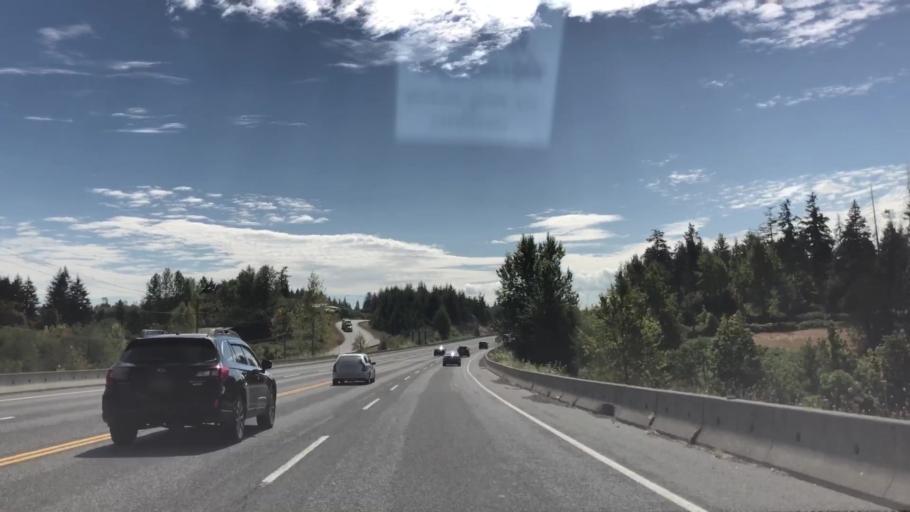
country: CA
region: British Columbia
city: Nanaimo
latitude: 49.1295
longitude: -123.8649
